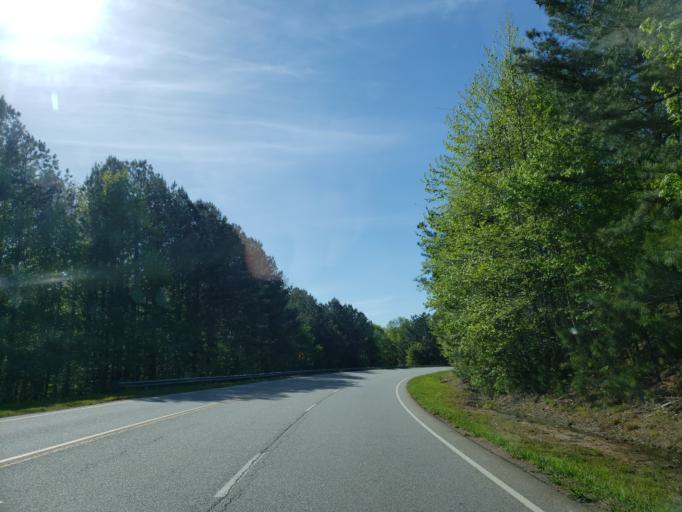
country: US
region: Georgia
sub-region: Haralson County
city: Tallapoosa
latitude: 33.7148
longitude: -85.2786
